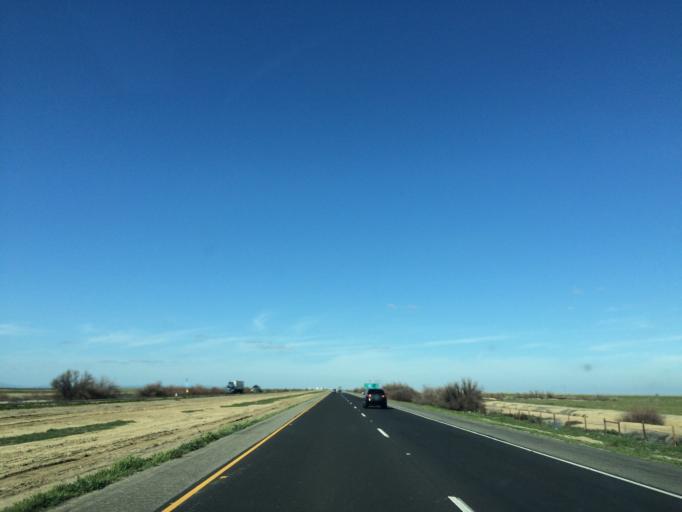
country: US
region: California
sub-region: Kern County
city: Lost Hills
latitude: 35.7386
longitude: -119.7442
